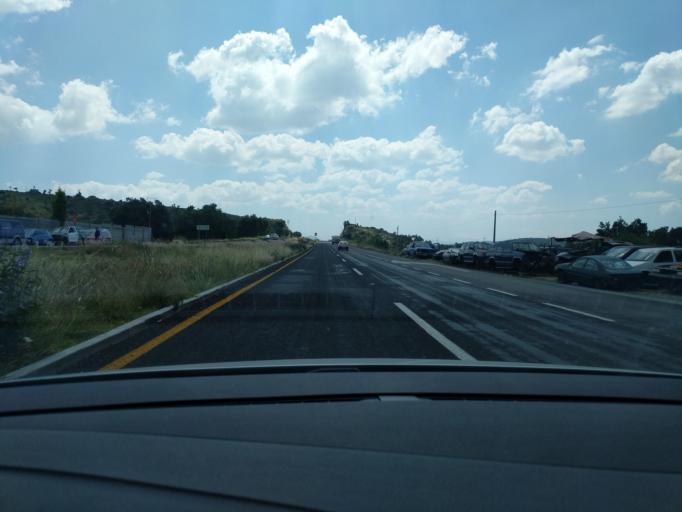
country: MX
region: Hidalgo
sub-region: Mineral de la Reforma
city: Rinconada de los Angeles
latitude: 19.9894
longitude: -98.7056
